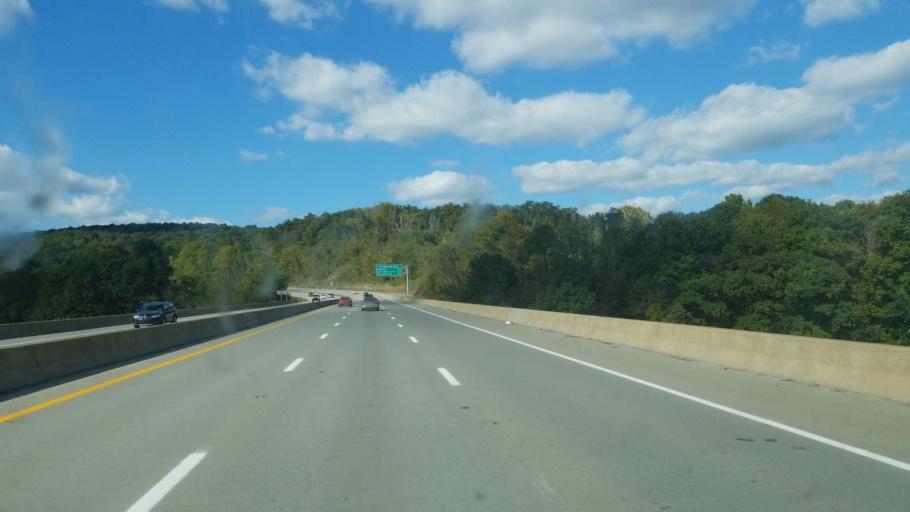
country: US
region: West Virginia
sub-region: Monongalia County
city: Westover
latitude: 39.5887
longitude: -79.9793
